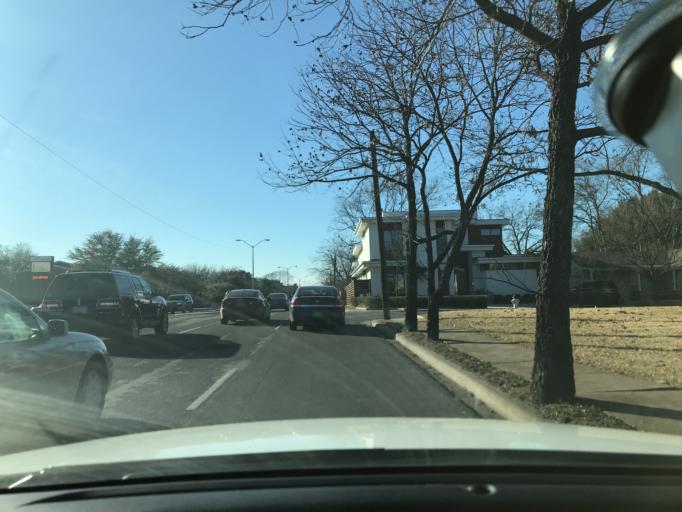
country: US
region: Texas
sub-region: Dallas County
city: Highland Park
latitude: 32.8366
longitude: -96.7619
